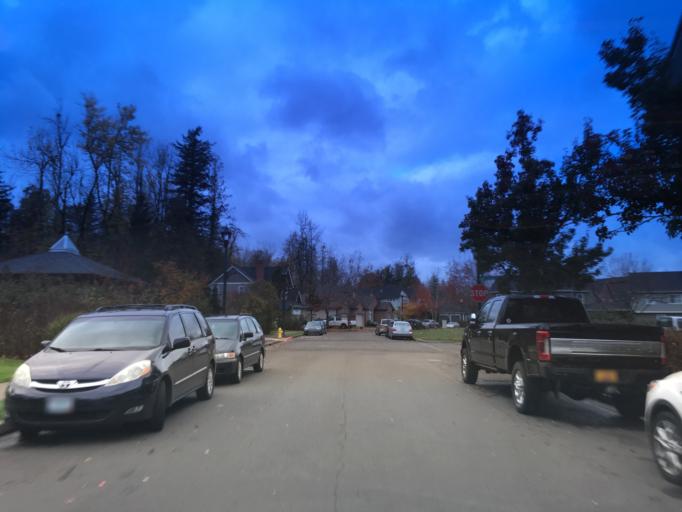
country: US
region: Oregon
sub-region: Multnomah County
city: Fairview
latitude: 45.5307
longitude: -122.4388
